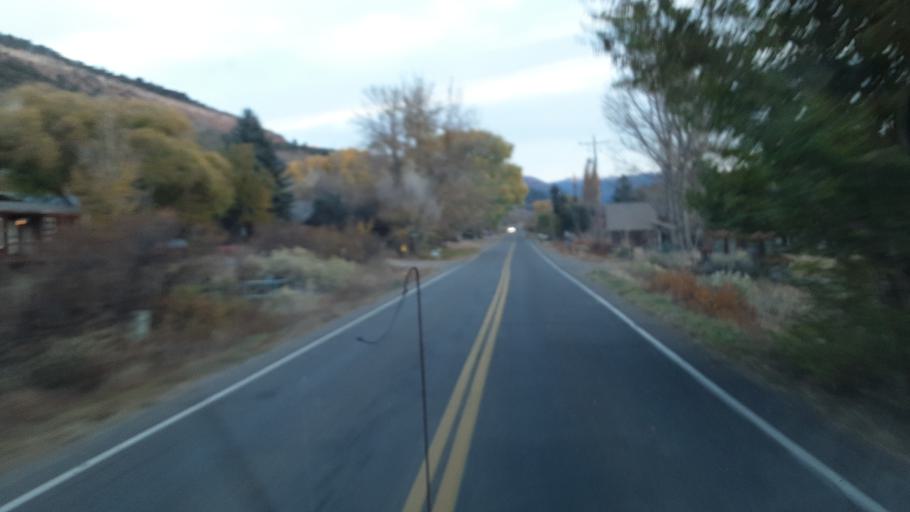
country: US
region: Colorado
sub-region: La Plata County
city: Durango
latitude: 37.3325
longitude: -107.8549
